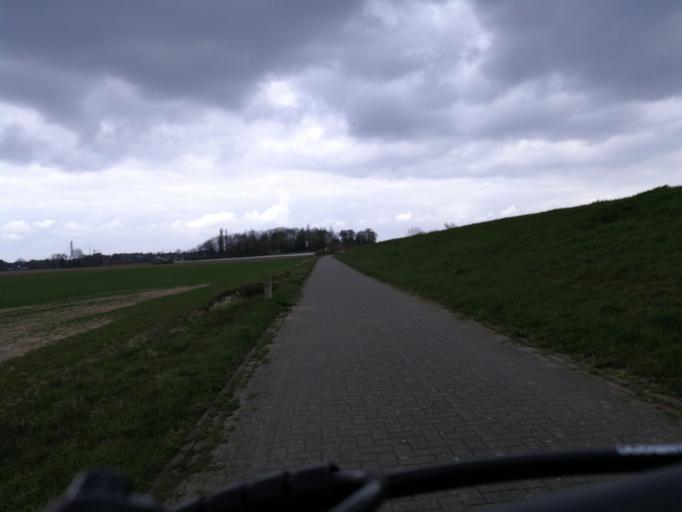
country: DE
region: North Rhine-Westphalia
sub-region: Regierungsbezirk Dusseldorf
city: Dusseldorf
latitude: 51.1544
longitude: 6.7893
